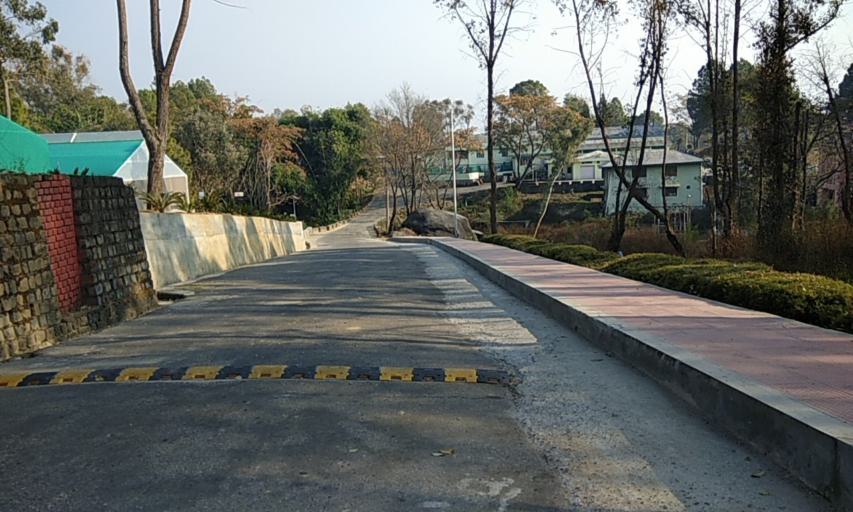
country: IN
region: Himachal Pradesh
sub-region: Kangra
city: Palampur
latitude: 32.1068
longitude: 76.5558
